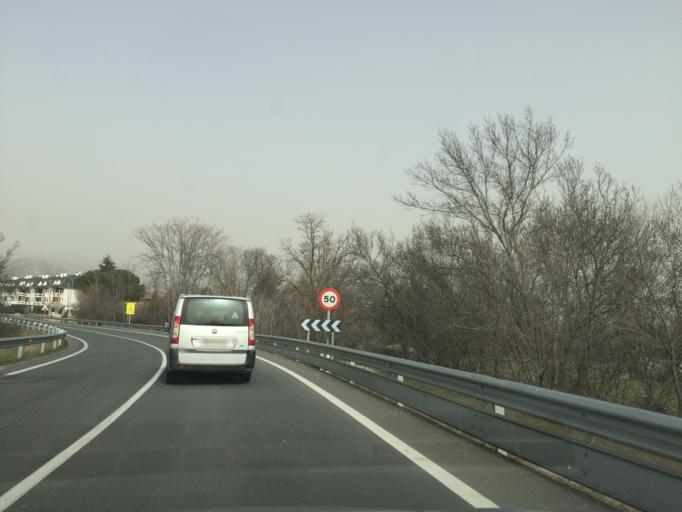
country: ES
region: Madrid
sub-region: Provincia de Madrid
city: Boalo
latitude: 40.6956
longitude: -3.9386
